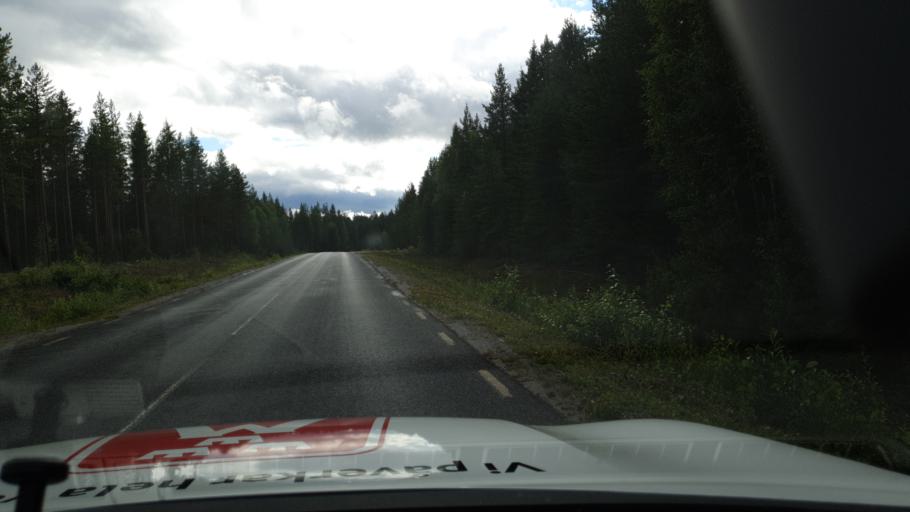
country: SE
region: Vaesterbotten
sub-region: Skelleftea Kommun
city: Soedra Bergsbyn
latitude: 64.5916
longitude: 21.0496
